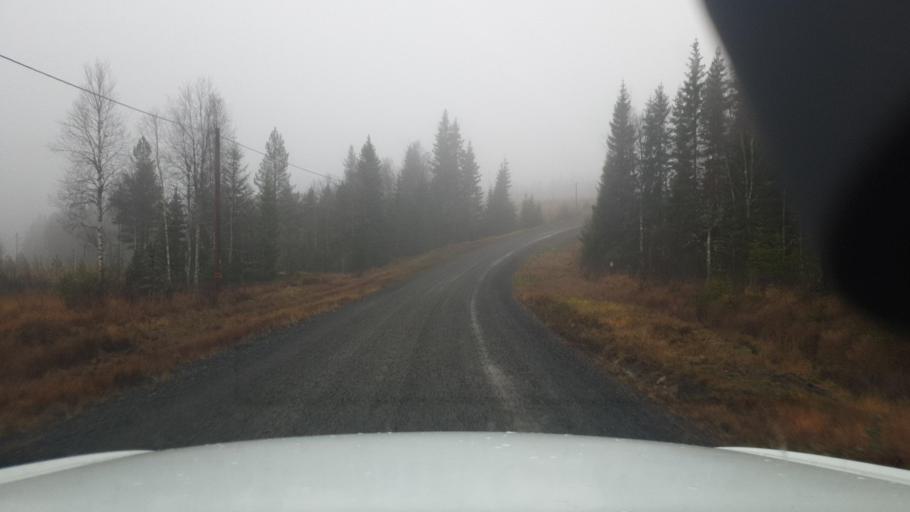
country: SE
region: Vaermland
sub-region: Torsby Kommun
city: Torsby
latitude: 60.1630
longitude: 12.6138
